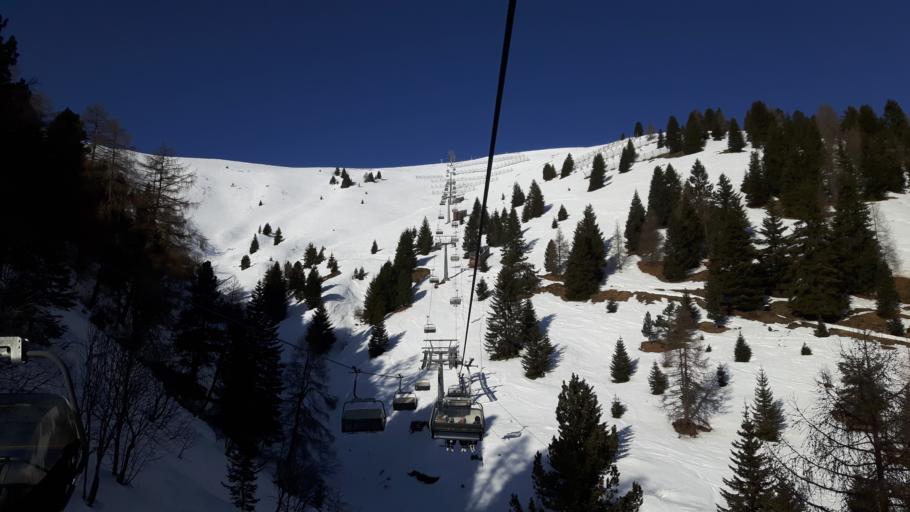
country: IT
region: Trentino-Alto Adige
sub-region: Provincia di Trento
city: Predazzo
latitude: 46.3435
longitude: 11.5673
